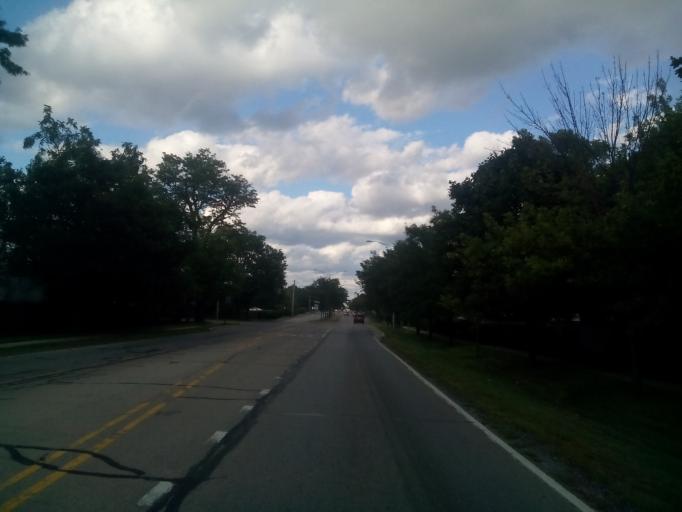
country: US
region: Illinois
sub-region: Will County
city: Romeoville
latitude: 41.6951
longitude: -88.1499
